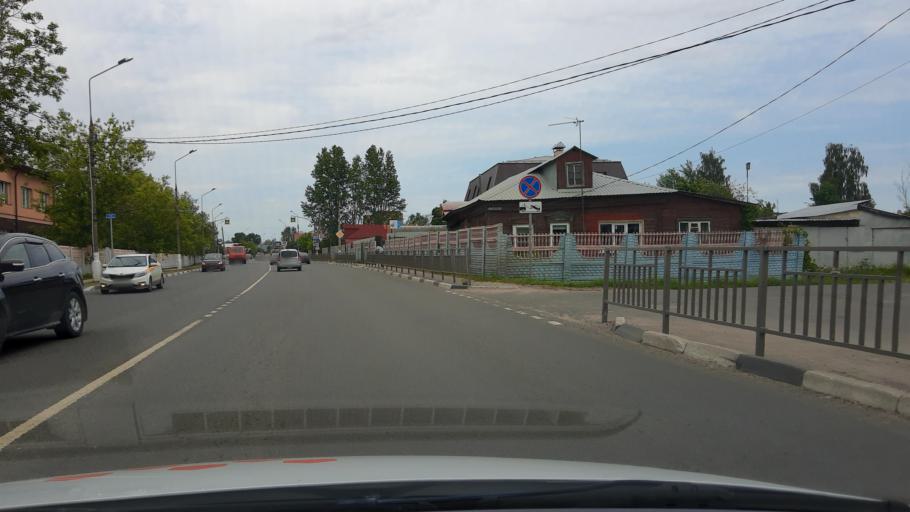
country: RU
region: Moskovskaya
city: Noginsk
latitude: 55.8677
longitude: 38.4397
